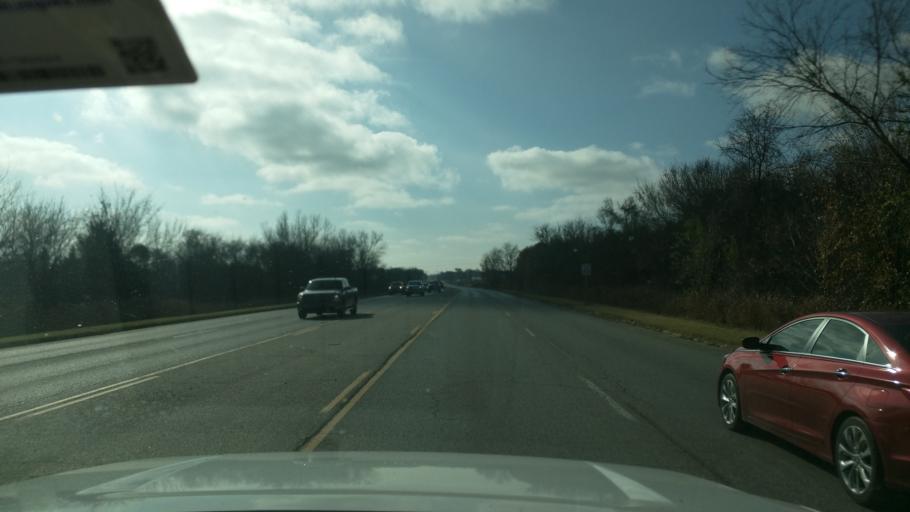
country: US
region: Oklahoma
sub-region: Washington County
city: Dewey
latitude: 36.7820
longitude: -95.9354
